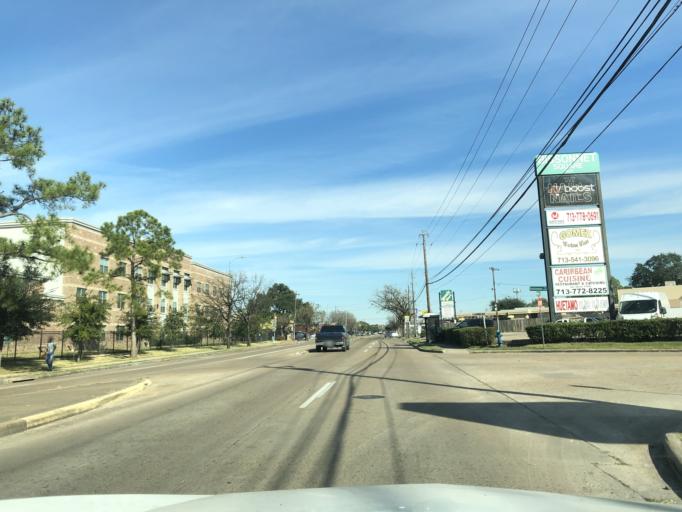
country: US
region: Texas
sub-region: Harris County
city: Bellaire
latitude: 29.6845
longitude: -95.5132
